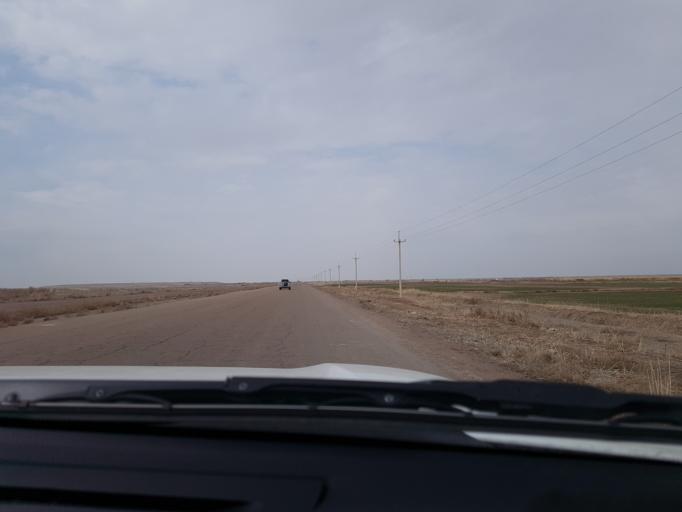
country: TM
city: Akdepe
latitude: 41.7421
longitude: 58.7569
